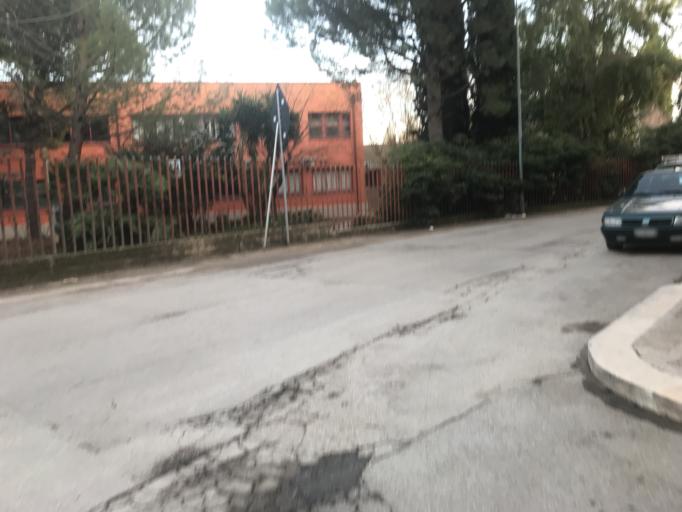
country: IT
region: Apulia
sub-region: Provincia di Bari
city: Corato
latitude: 41.1490
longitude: 16.4174
